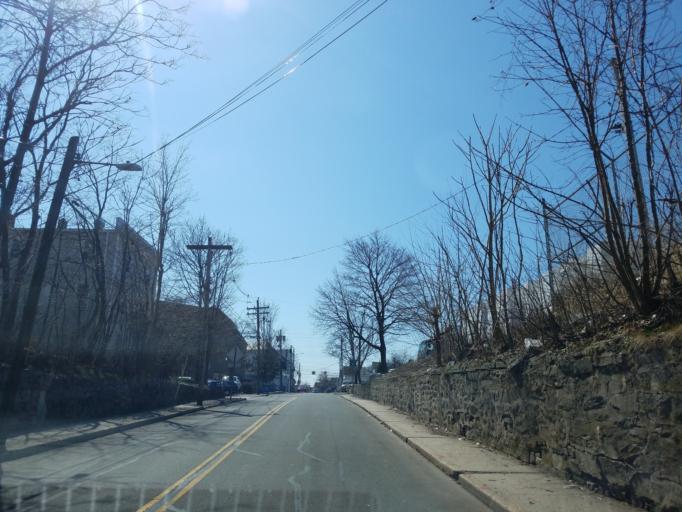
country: US
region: Connecticut
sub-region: Fairfield County
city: East Norwalk
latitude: 41.1021
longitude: -73.4074
